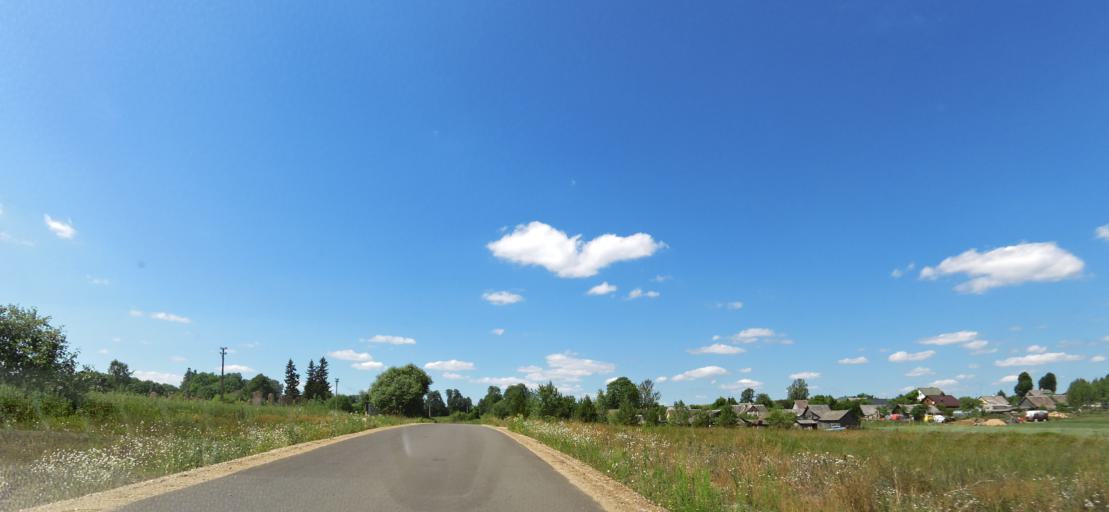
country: LT
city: Nemencine
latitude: 54.8743
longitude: 25.5459
